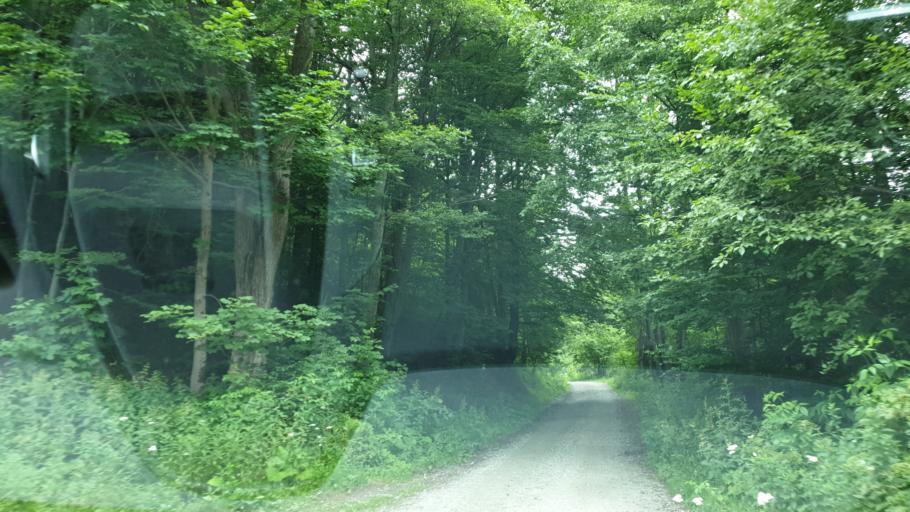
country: RO
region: Hunedoara
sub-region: Comuna Uricani
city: Uricani
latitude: 45.3031
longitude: 22.9884
